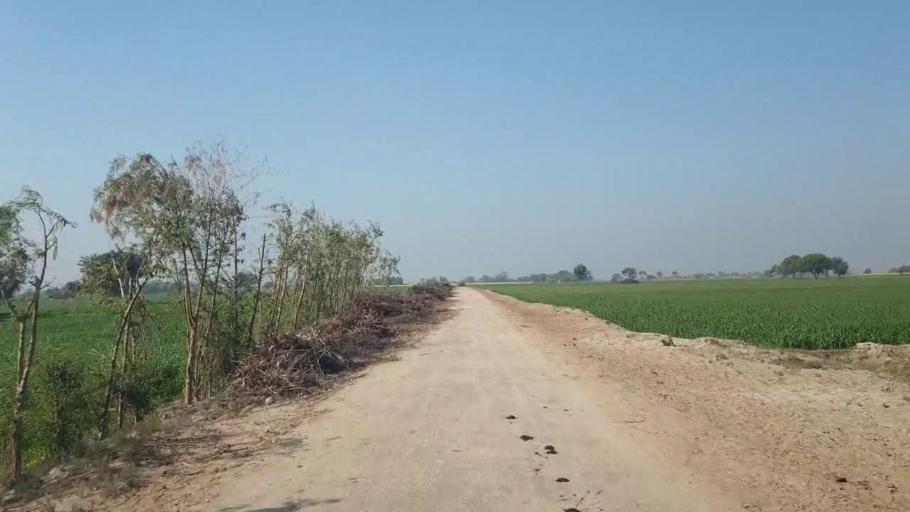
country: PK
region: Sindh
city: Shahdadpur
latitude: 25.9537
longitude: 68.5414
